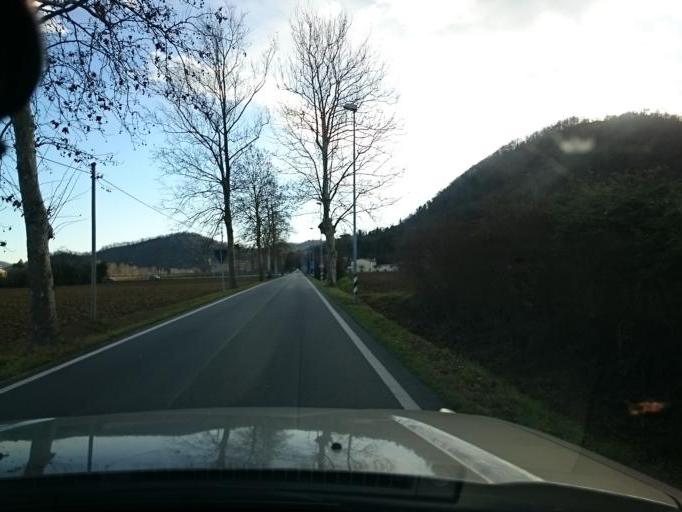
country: IT
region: Veneto
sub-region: Provincia di Padova
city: San Biagio
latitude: 45.3709
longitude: 11.7363
